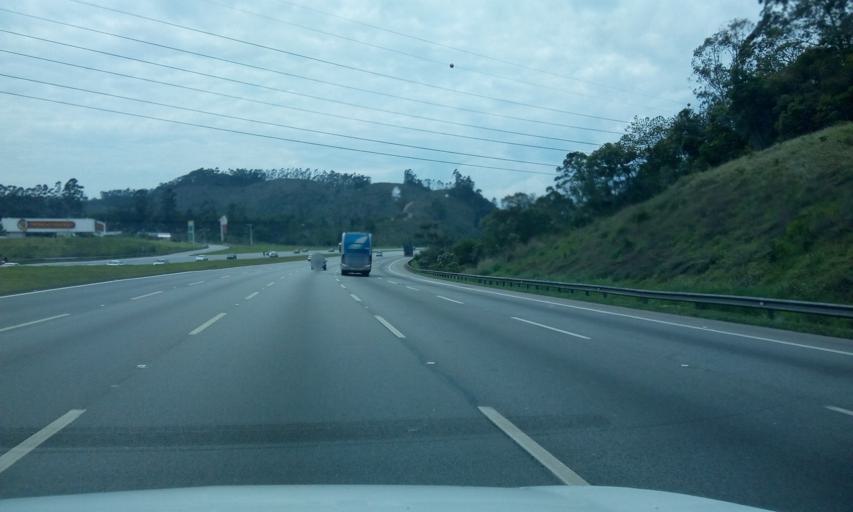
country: BR
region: Sao Paulo
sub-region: Caieiras
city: Caieiras
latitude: -23.3514
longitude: -46.8006
